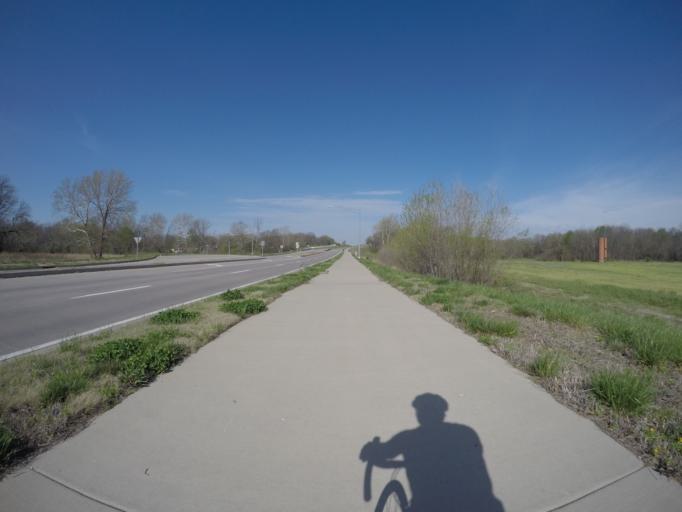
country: US
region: Missouri
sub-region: Cass County
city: Raymore
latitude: 38.8558
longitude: -94.4711
